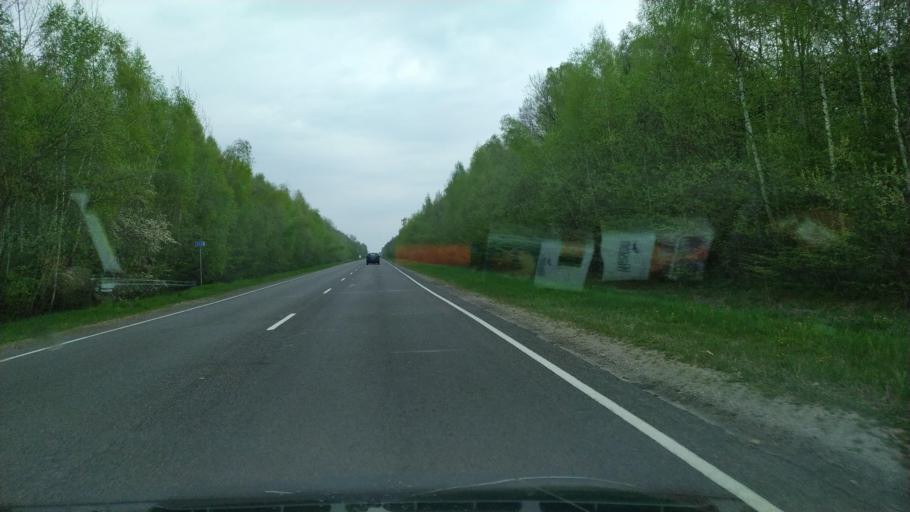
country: BY
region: Brest
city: Horad Kobryn
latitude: 52.3067
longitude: 24.5317
